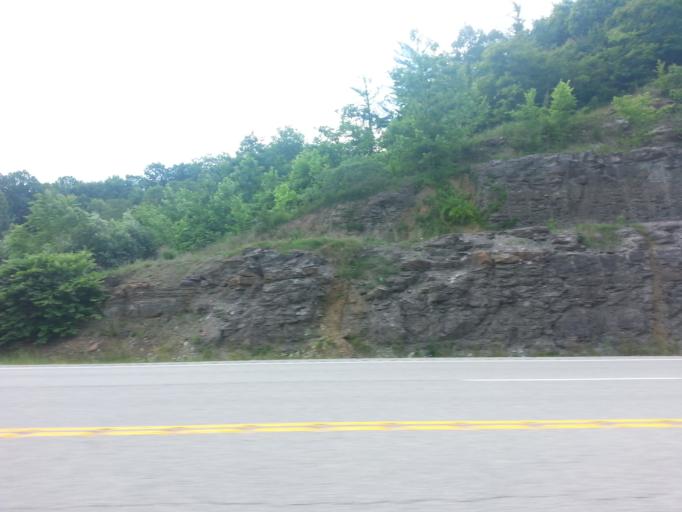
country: US
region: Virginia
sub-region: Lee County
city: Jonesville
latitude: 36.7668
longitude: -83.2019
